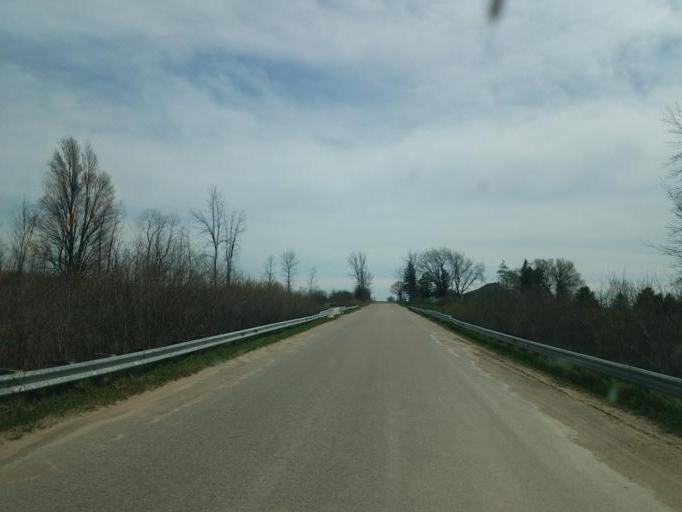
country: US
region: Michigan
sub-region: Gladwin County
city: Gladwin
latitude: 44.0553
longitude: -84.4676
